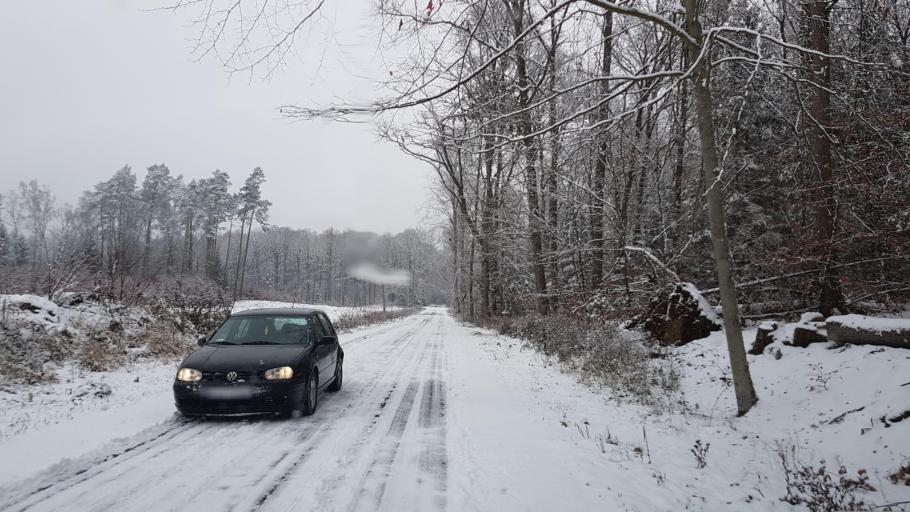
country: PL
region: West Pomeranian Voivodeship
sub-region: Powiat lobeski
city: Resko
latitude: 53.7883
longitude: 15.5322
